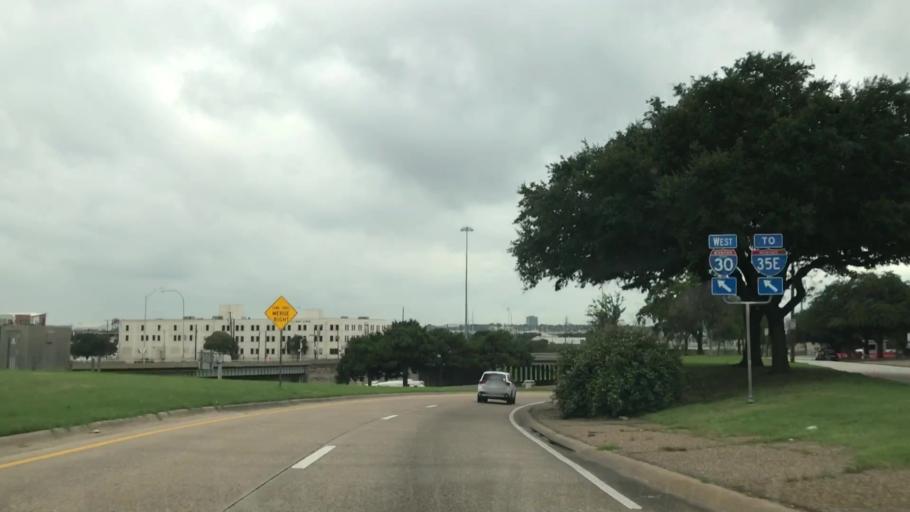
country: US
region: Texas
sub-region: Dallas County
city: Dallas
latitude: 32.7741
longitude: -96.7971
